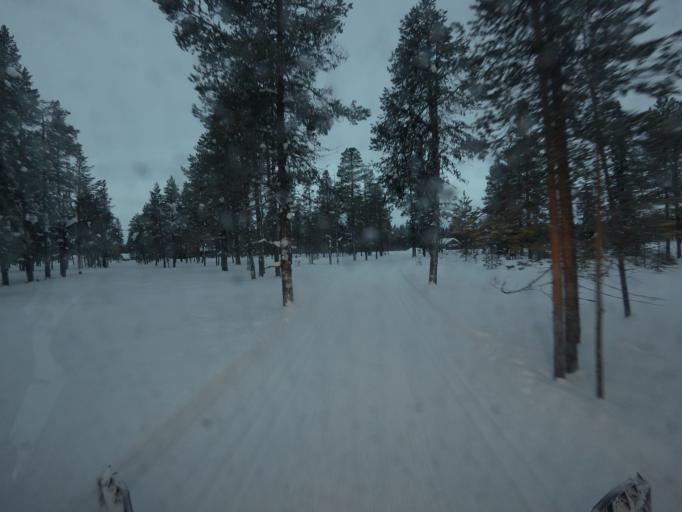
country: FI
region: Lapland
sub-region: Tunturi-Lappi
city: Kolari
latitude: 67.6241
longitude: 24.1747
